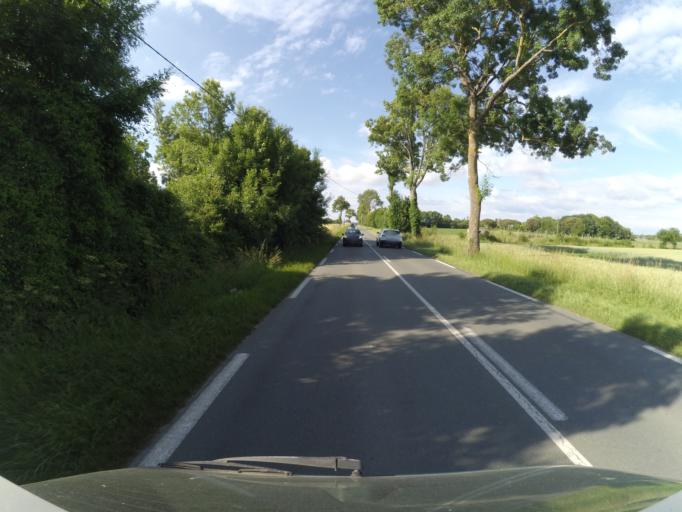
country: FR
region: Poitou-Charentes
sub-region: Departement de la Charente-Maritime
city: Le Gua
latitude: 45.7475
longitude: -0.9488
